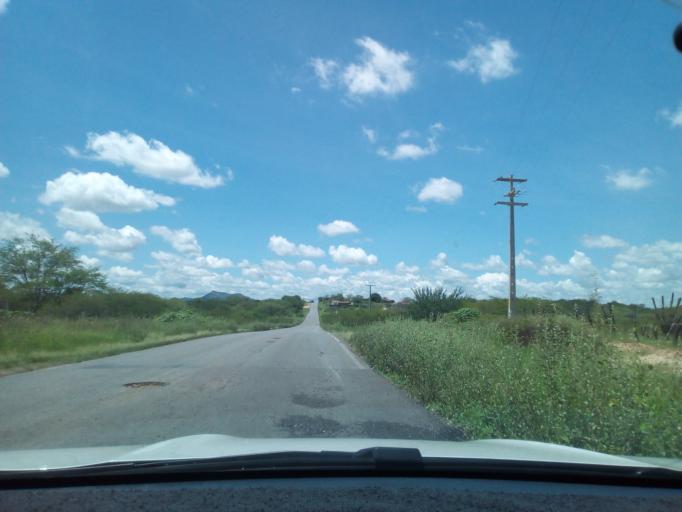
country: BR
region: Rio Grande do Norte
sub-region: Caico
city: Caico
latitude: -6.4986
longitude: -37.0749
